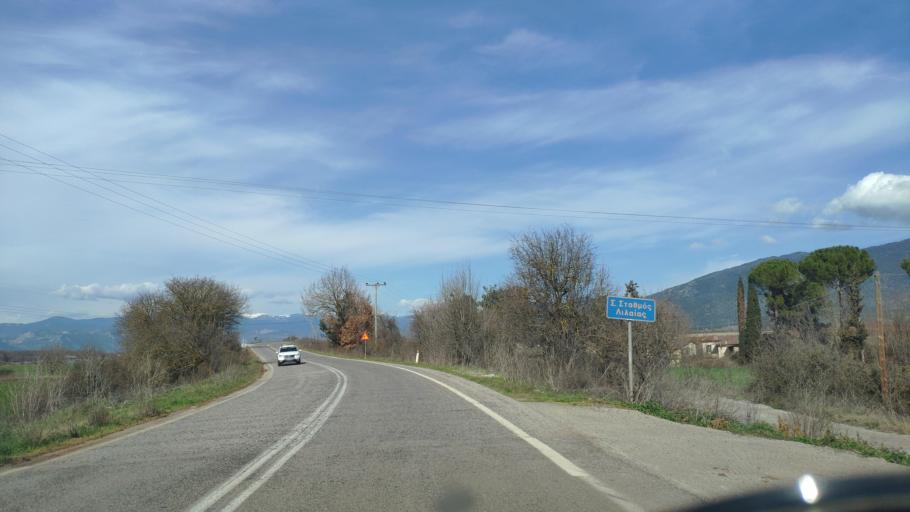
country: GR
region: Central Greece
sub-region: Nomos Fthiotidos
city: Amfikleia
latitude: 38.6684
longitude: 22.5457
